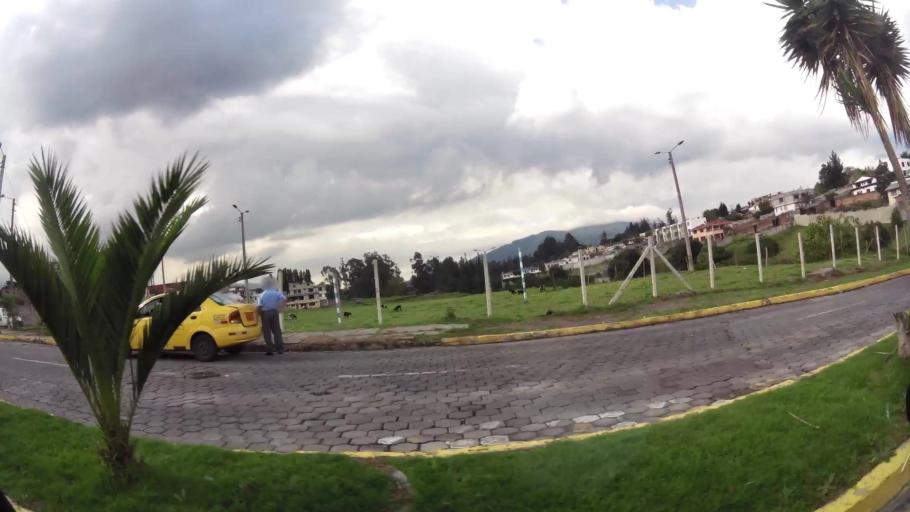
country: EC
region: Pichincha
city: Sangolqui
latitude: -0.3276
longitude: -78.4606
